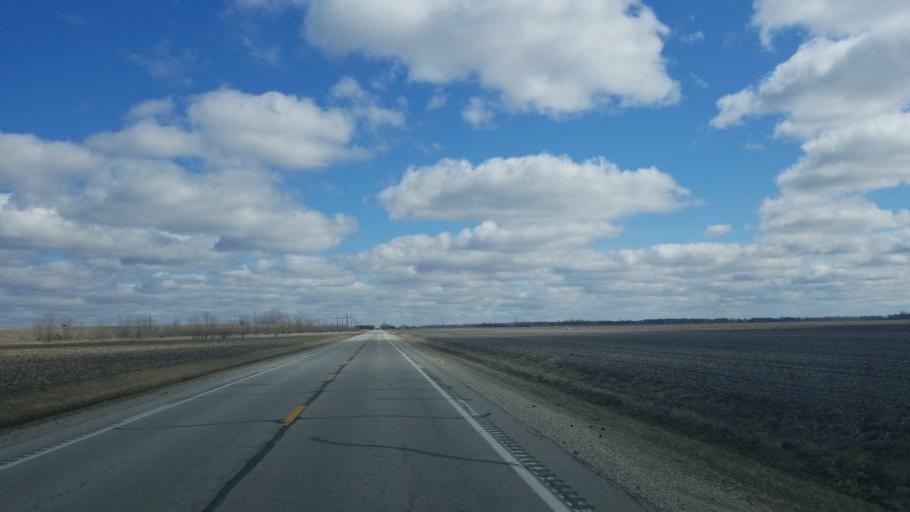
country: US
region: Illinois
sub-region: Douglas County
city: Villa Grove
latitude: 39.7921
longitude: -88.0627
